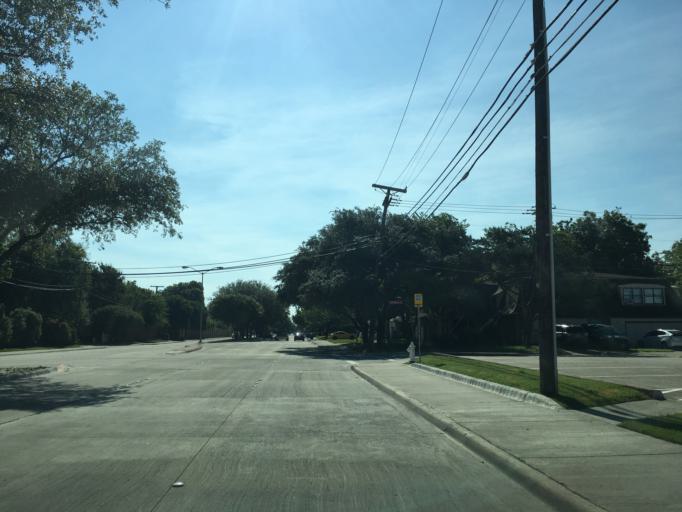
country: US
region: Texas
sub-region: Dallas County
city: Farmers Branch
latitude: 32.9243
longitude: -96.8795
